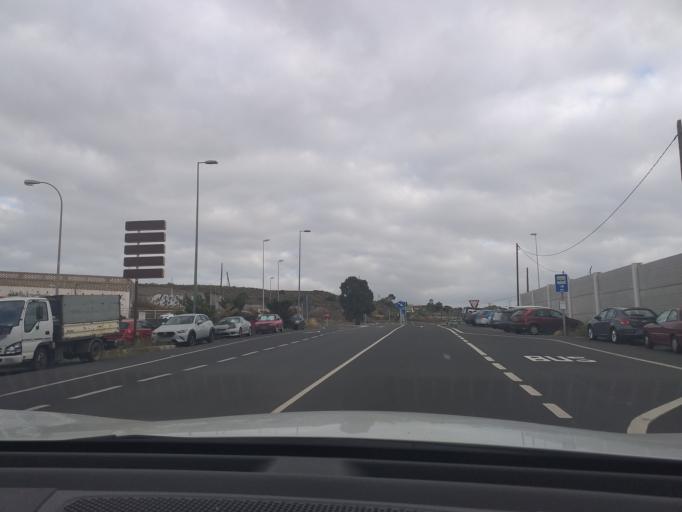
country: ES
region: Canary Islands
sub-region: Provincia de Las Palmas
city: Arucas
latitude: 28.1079
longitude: -15.4891
